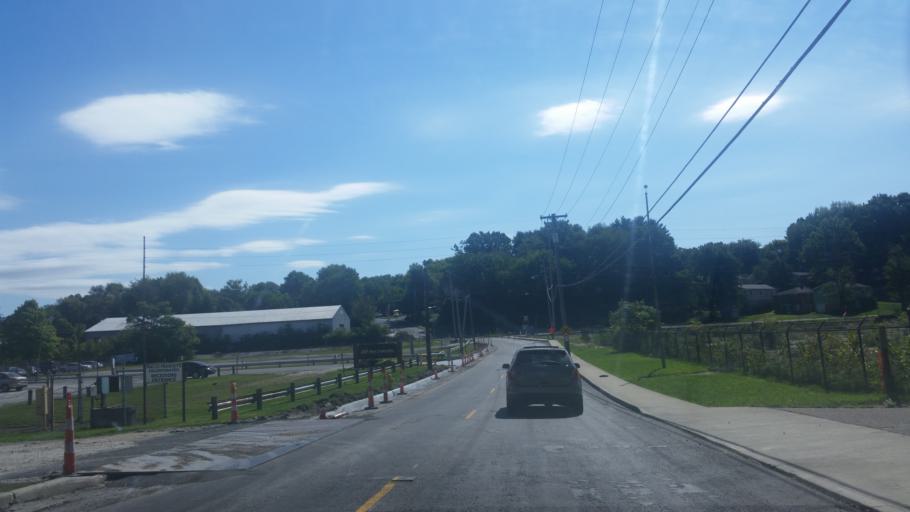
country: US
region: Ohio
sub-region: Summit County
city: Barberton
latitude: 41.0236
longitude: -81.5924
